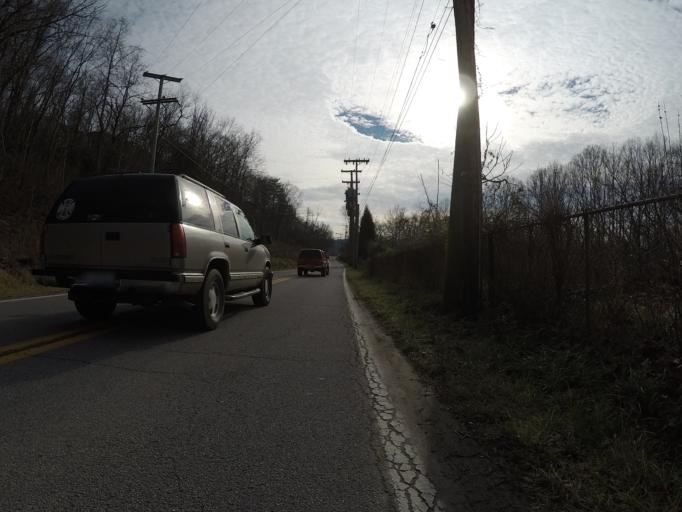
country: US
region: West Virginia
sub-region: Cabell County
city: Barboursville
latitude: 38.4134
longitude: -82.2950
